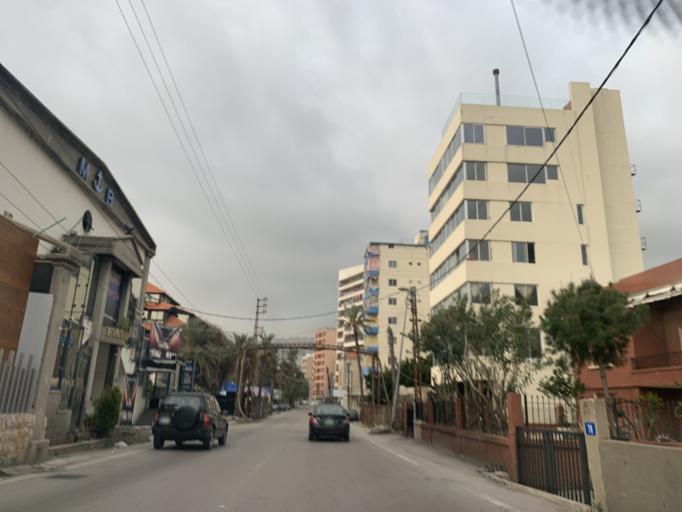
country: LB
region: Mont-Liban
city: Djounie
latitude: 34.0014
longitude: 35.6446
